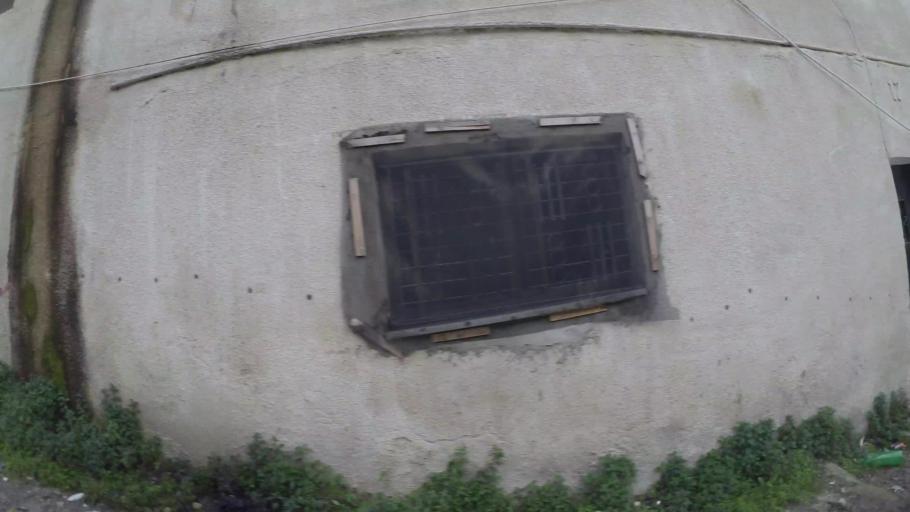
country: JO
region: Amman
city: Wadi as Sir
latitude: 31.9526
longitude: 35.8175
